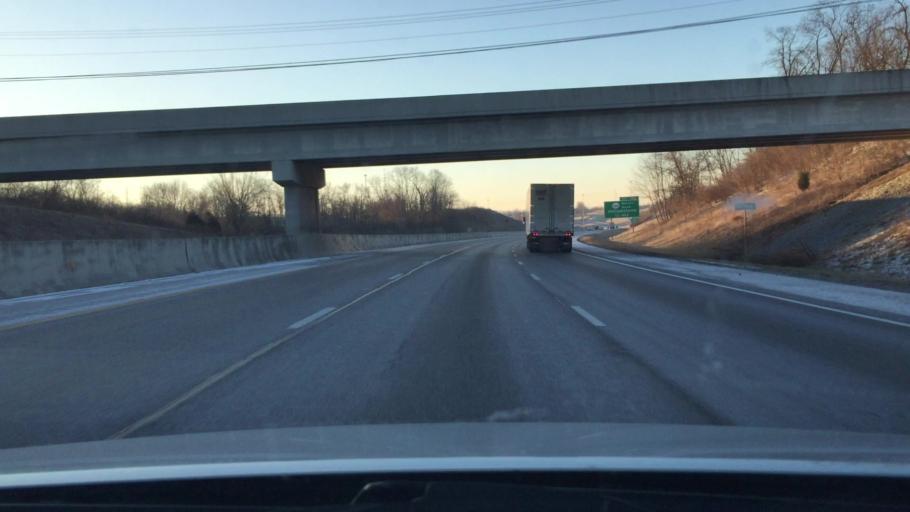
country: US
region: Kentucky
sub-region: Grant County
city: Dry Ridge
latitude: 38.6594
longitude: -84.5870
